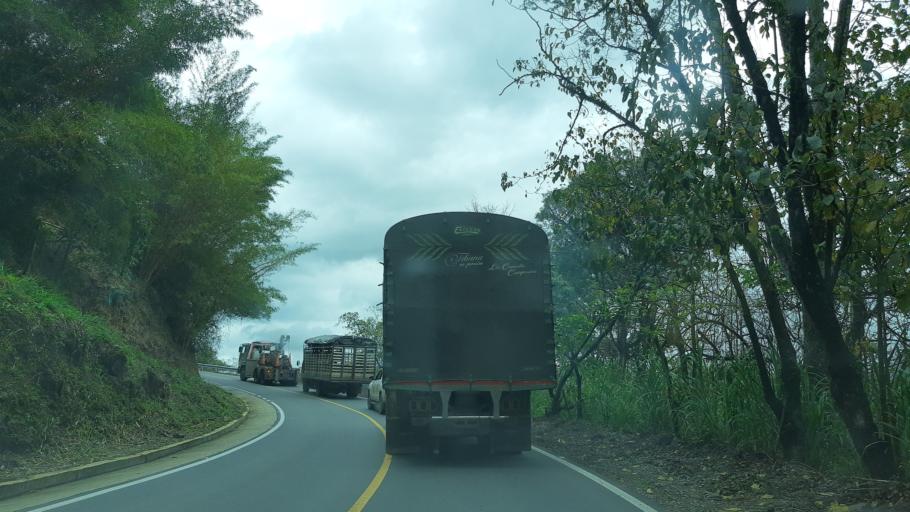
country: CO
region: Boyaca
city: Somondoco
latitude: 4.9797
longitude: -73.3408
